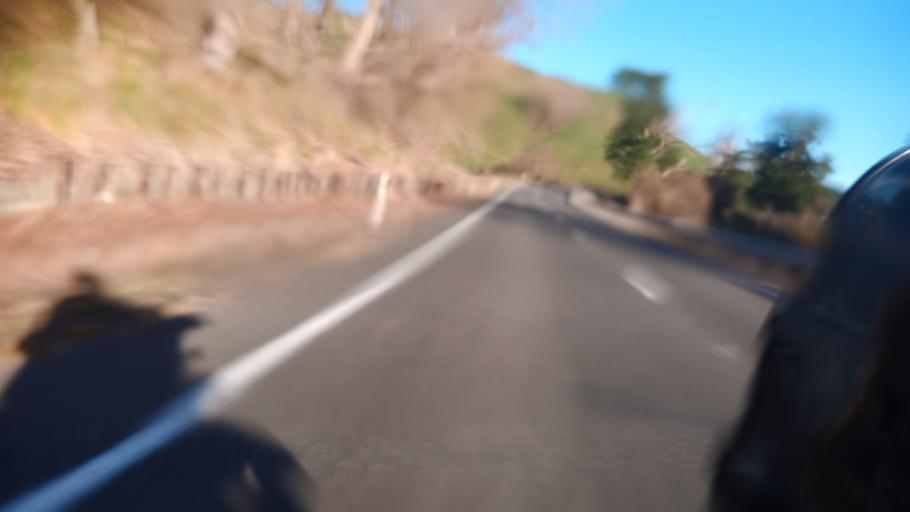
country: NZ
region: Hawke's Bay
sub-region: Wairoa District
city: Wairoa
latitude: -39.0159
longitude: 177.3544
